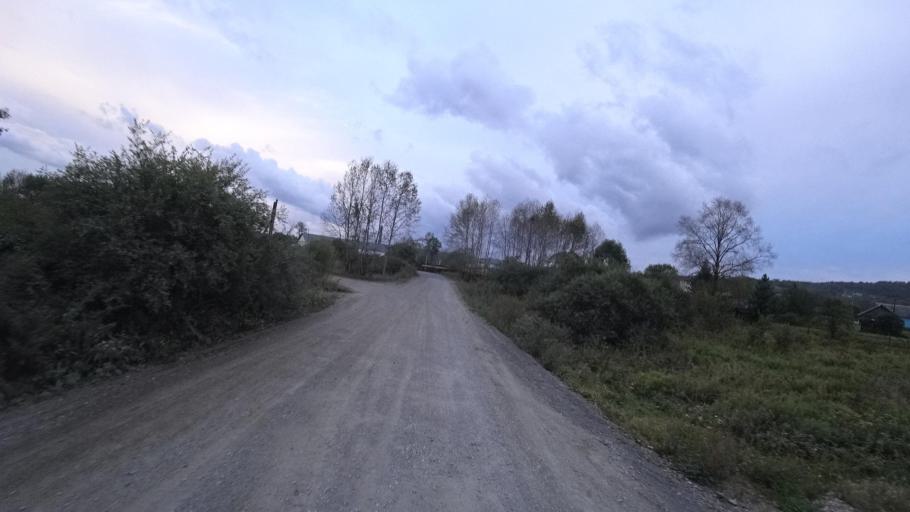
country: RU
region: Jewish Autonomous Oblast
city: Izvestkovyy
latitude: 48.9899
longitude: 131.5520
